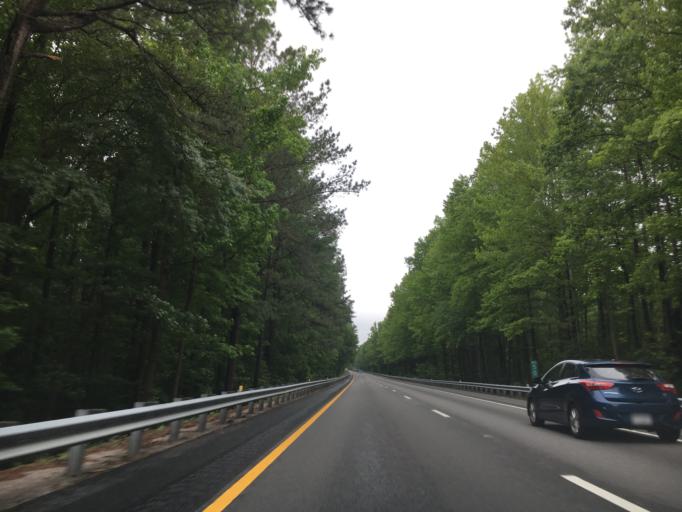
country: US
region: Virginia
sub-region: Dinwiddie County
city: Dinwiddie
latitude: 37.0547
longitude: -77.6052
